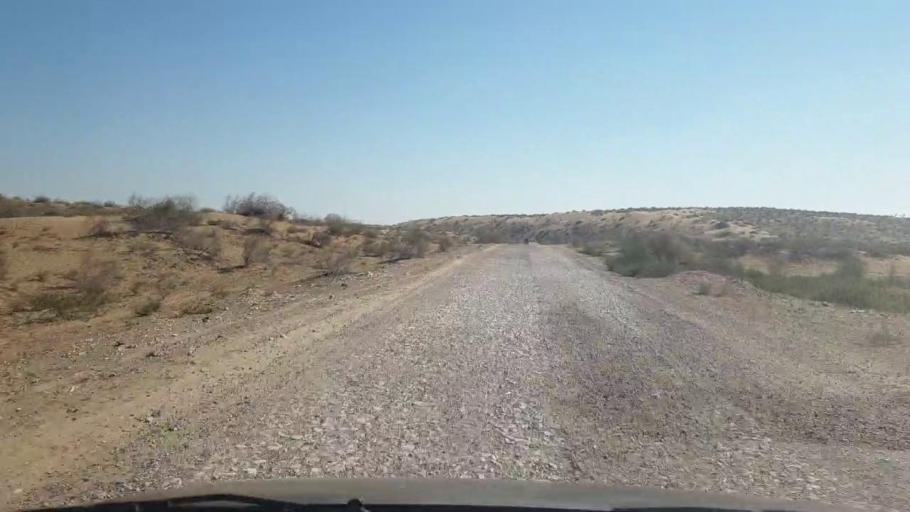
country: PK
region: Sindh
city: Bozdar
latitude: 27.0156
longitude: 68.7364
